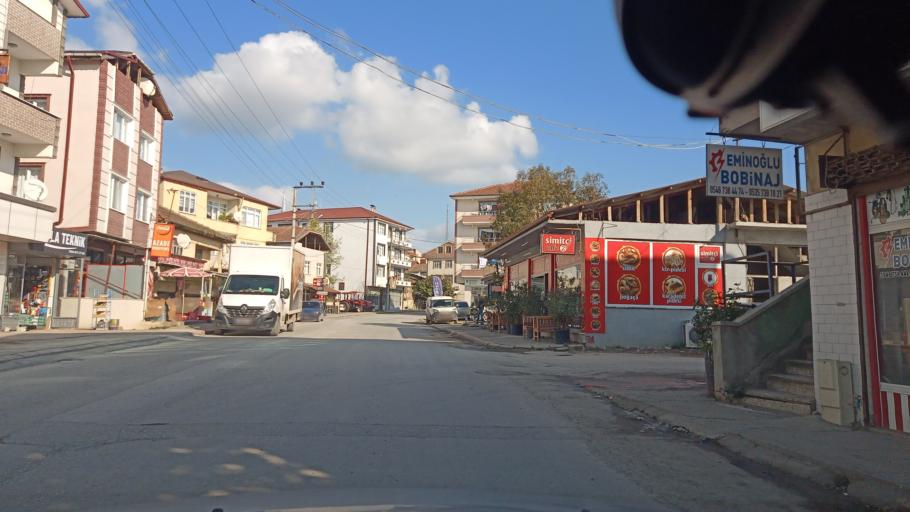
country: TR
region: Sakarya
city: Kaynarca
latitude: 41.0300
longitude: 30.3064
